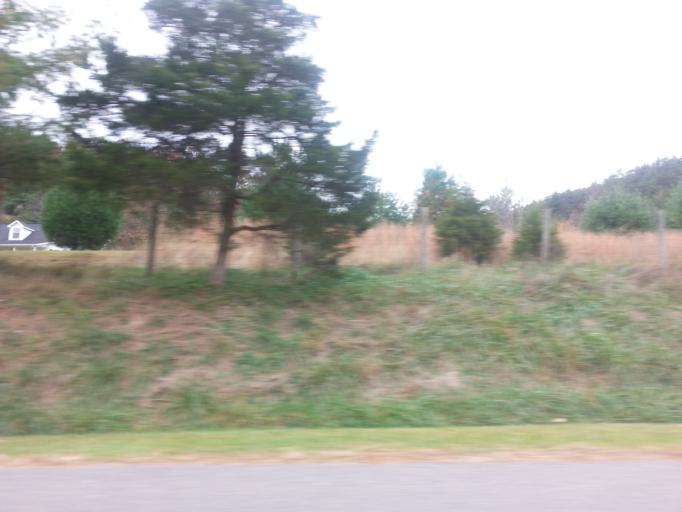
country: US
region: Virginia
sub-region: Bland County
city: Bland
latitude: 37.0553
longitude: -81.0482
